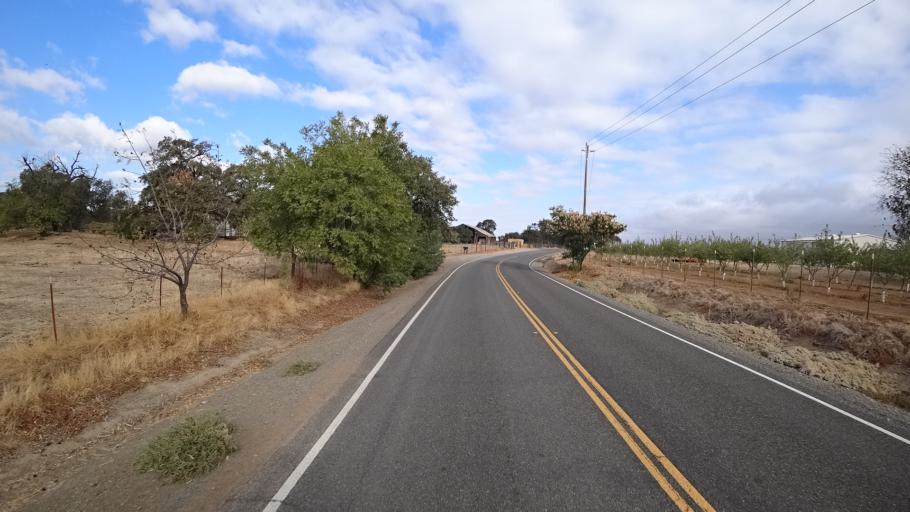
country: US
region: California
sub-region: Yolo County
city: Esparto
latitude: 38.7158
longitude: -122.0472
